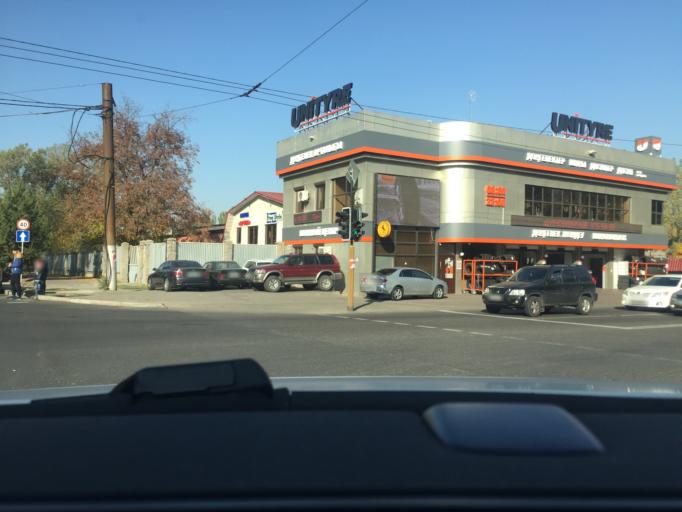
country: KZ
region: Almaty Qalasy
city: Almaty
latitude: 43.2438
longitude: 76.9082
